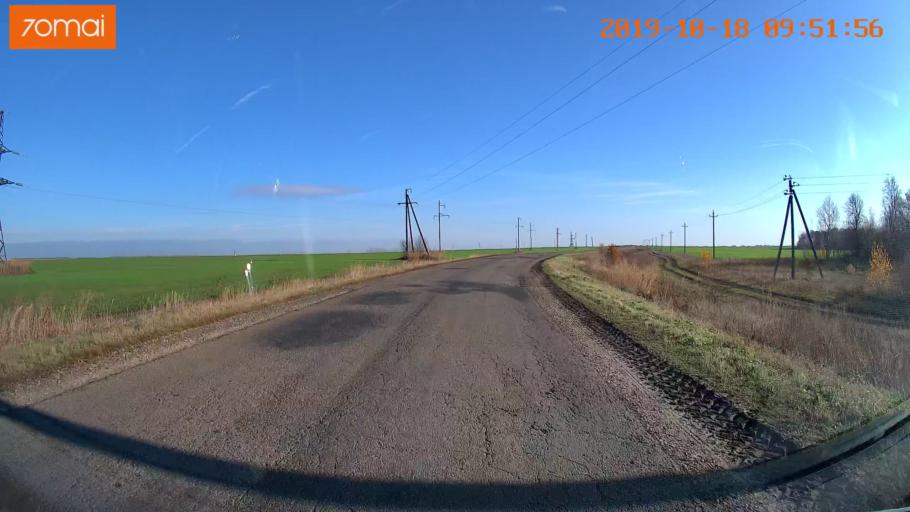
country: RU
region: Tula
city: Kazachka
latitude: 53.3465
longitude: 38.3003
